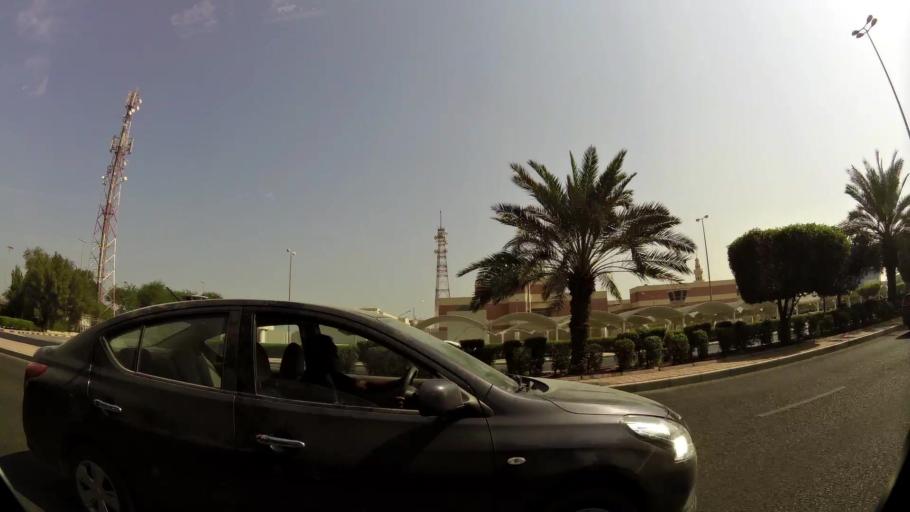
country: KW
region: Al Ahmadi
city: Al Fintas
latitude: 29.1689
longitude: 48.1228
